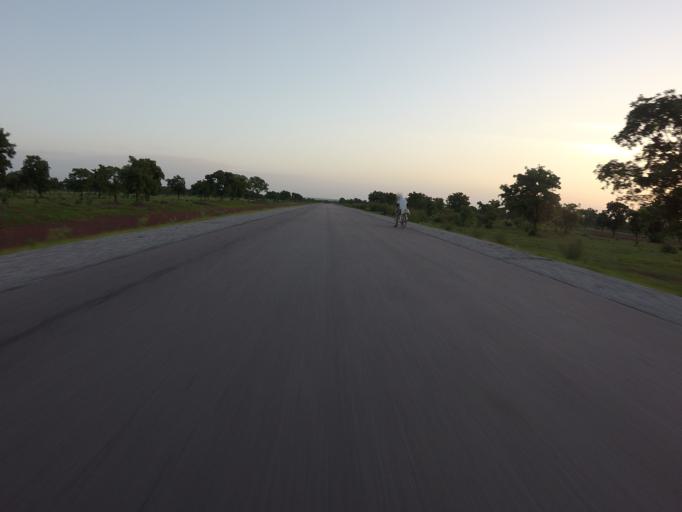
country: GH
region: Northern
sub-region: Yendi
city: Yendi
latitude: 9.9437
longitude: -0.1640
